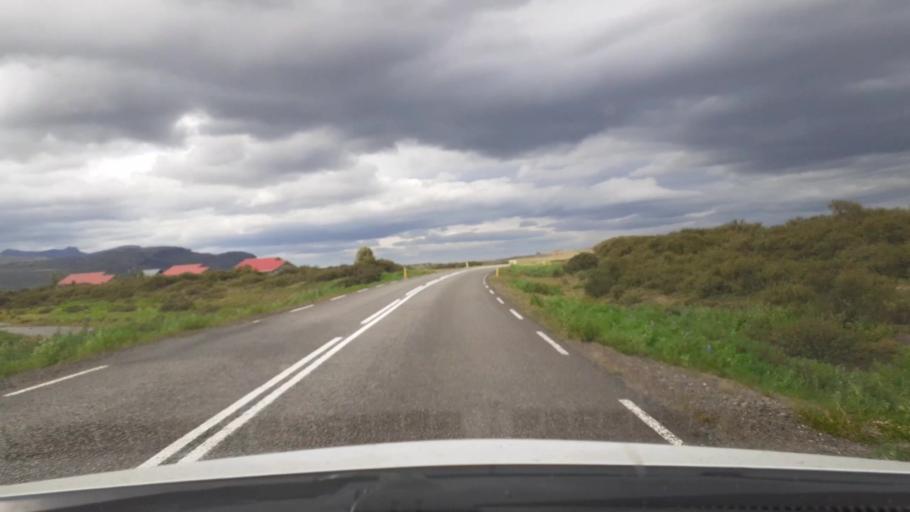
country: IS
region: West
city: Borgarnes
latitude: 64.5432
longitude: -21.6260
